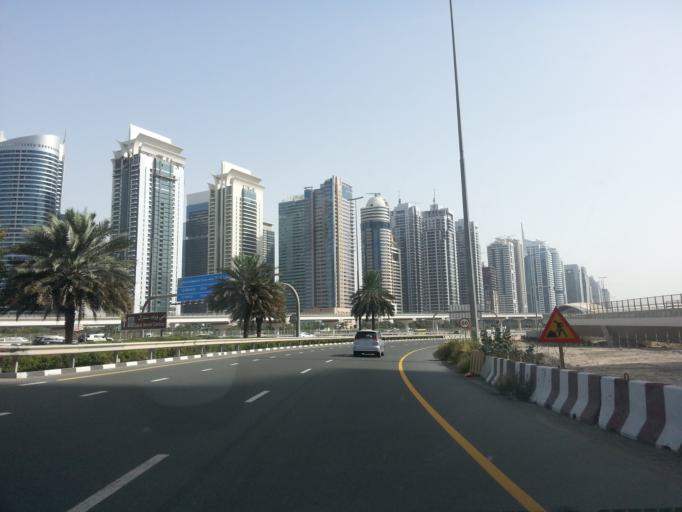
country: AE
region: Dubai
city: Dubai
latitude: 25.0848
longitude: 55.1509
